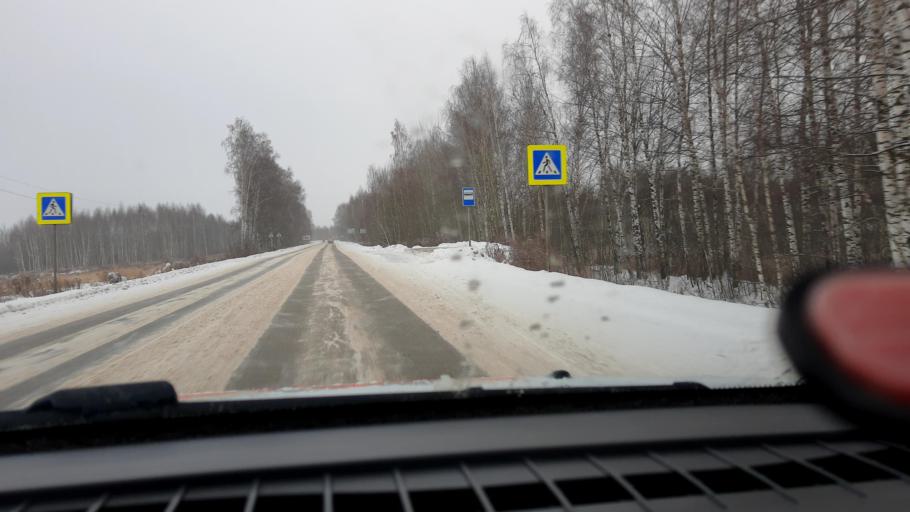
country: RU
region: Nizjnij Novgorod
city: Afonino
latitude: 56.3162
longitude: 44.2159
